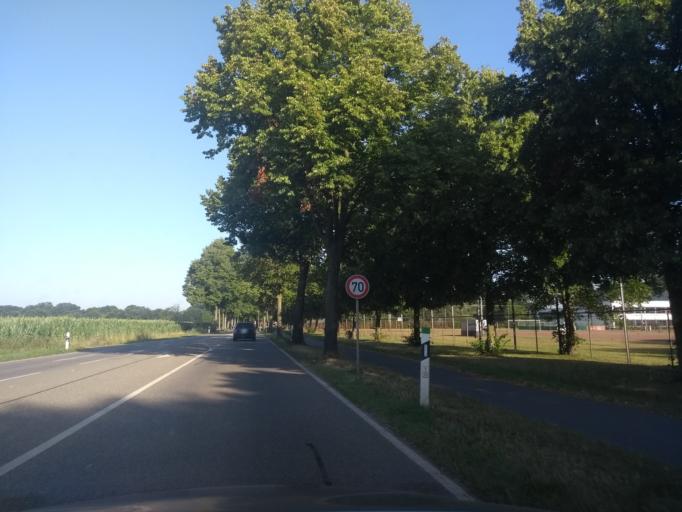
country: DE
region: North Rhine-Westphalia
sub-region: Regierungsbezirk Dusseldorf
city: Kleve
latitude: 51.8021
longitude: 6.1270
